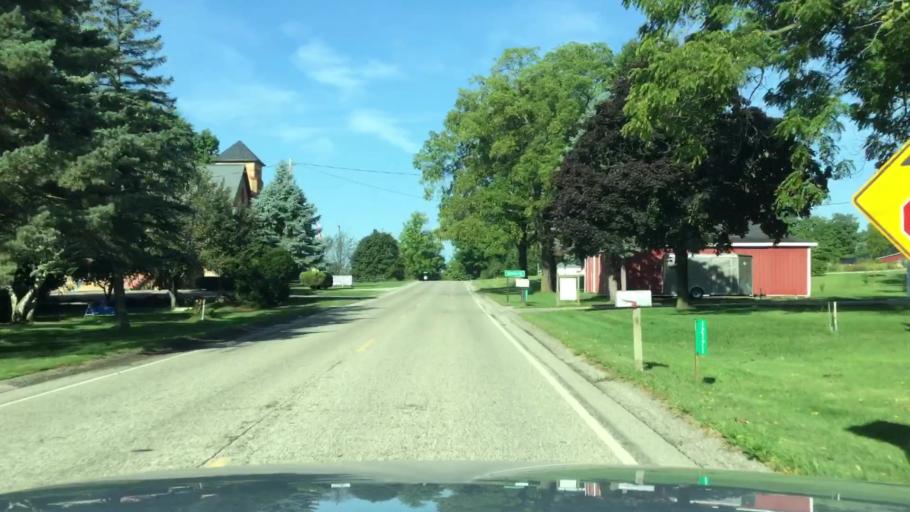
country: US
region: Michigan
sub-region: Lenawee County
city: Hudson
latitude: 41.9277
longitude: -84.4179
